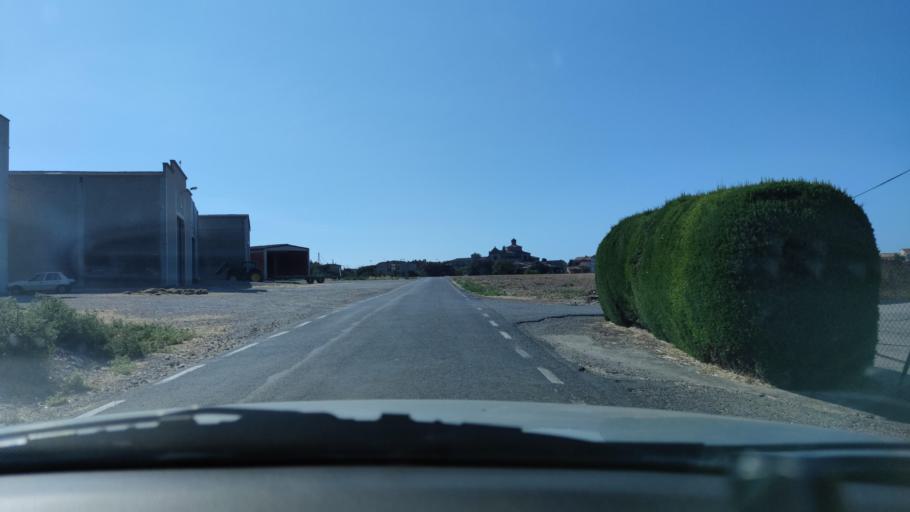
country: ES
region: Catalonia
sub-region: Provincia de Lleida
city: Ivorra
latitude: 41.7300
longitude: 1.3652
